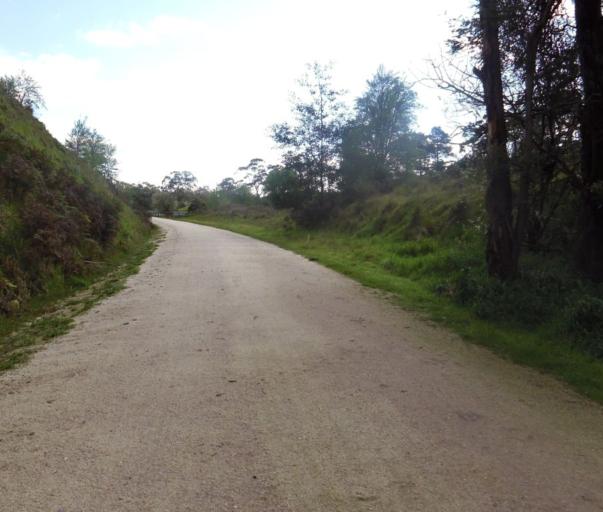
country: AU
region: Victoria
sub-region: Bass Coast
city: North Wonthaggi
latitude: -38.5627
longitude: 145.9594
